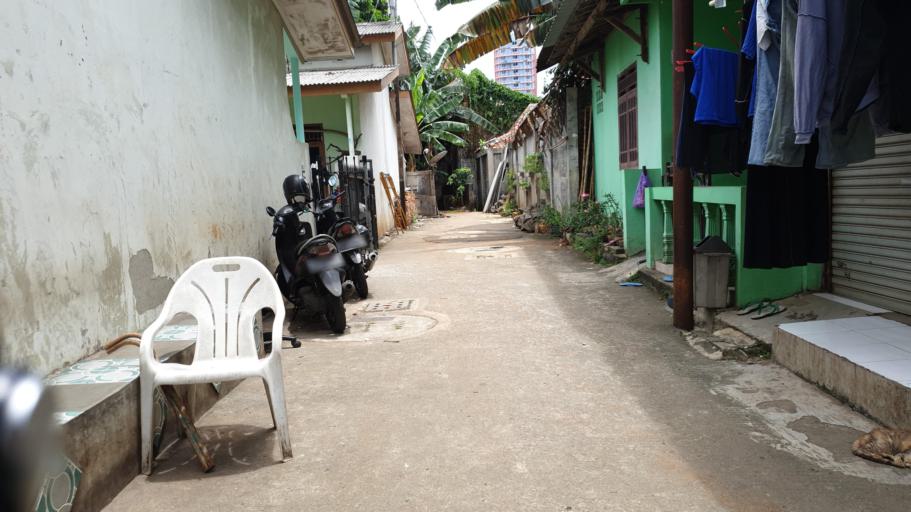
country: ID
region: West Java
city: Pamulang
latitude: -6.2961
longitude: 106.7816
